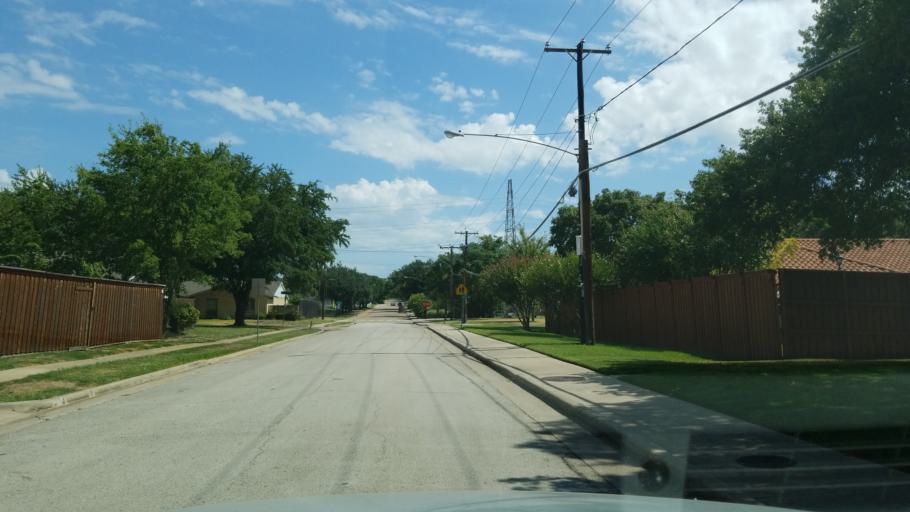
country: US
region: Texas
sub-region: Dallas County
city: Addison
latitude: 32.9596
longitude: -96.7799
